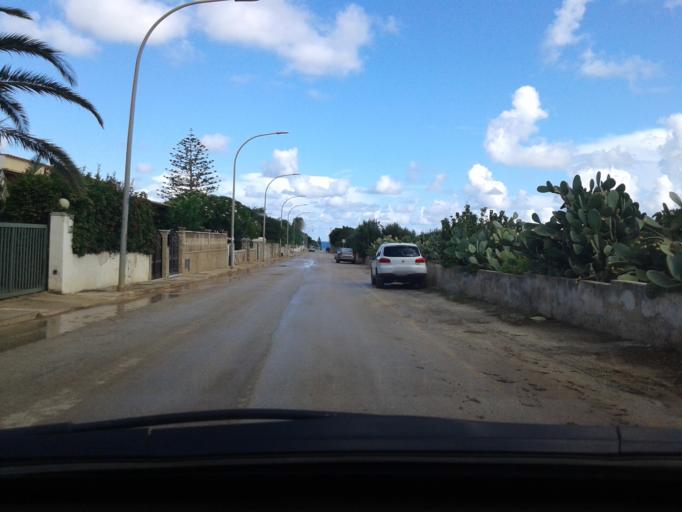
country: IT
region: Sicily
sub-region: Trapani
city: San Vito Lo Capo
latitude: 38.1692
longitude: 12.7422
